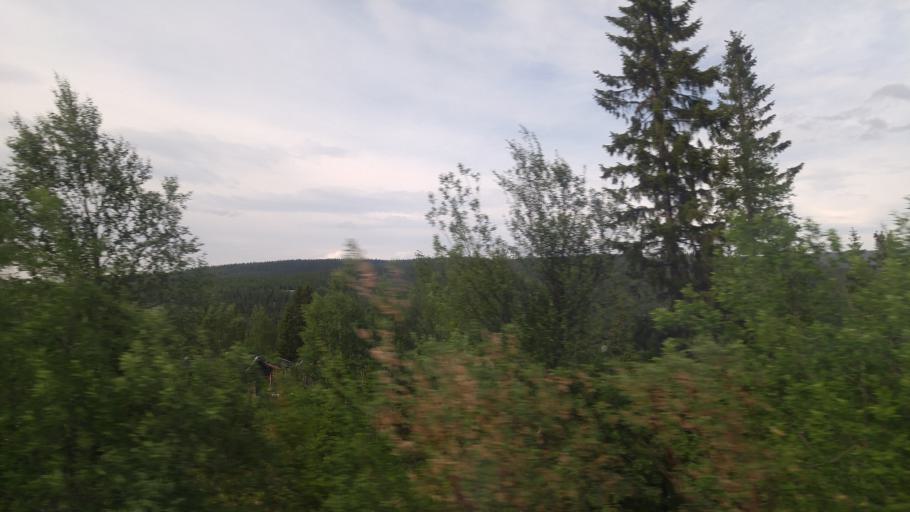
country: SE
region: Jaemtland
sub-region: Are Kommun
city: Are
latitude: 63.3952
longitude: 12.8320
